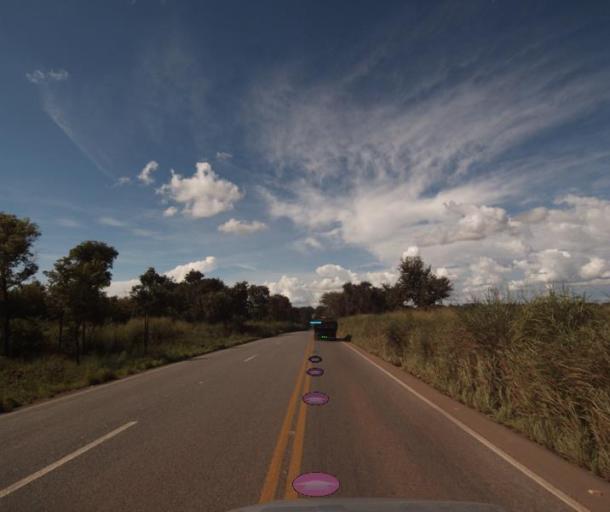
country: BR
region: Goias
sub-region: Porangatu
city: Porangatu
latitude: -13.0745
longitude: -49.1872
